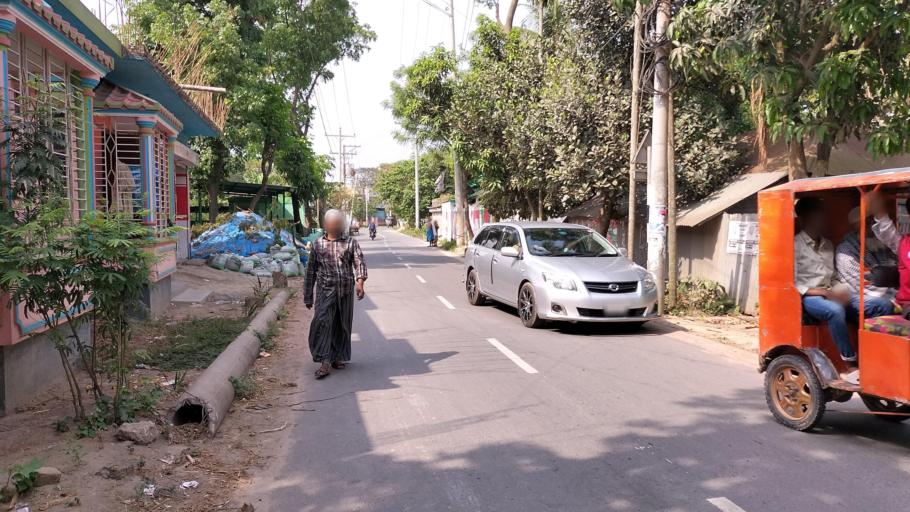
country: BD
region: Dhaka
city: Azimpur
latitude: 23.7534
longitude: 90.2913
